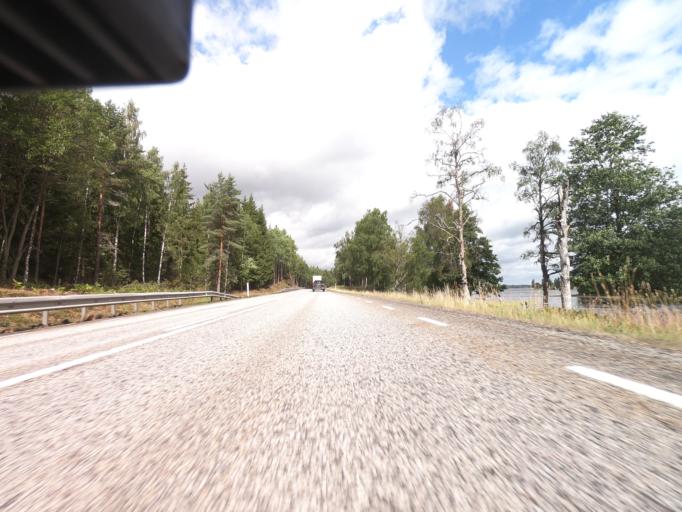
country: SE
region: Joenkoeping
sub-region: Vaggeryds Kommun
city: Vaggeryd
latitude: 57.5426
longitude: 14.2653
